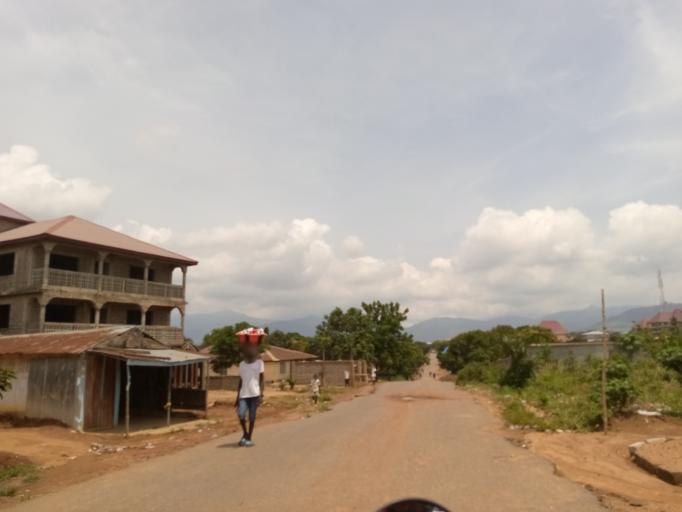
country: SL
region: Western Area
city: Waterloo
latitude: 8.3348
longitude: -13.0358
